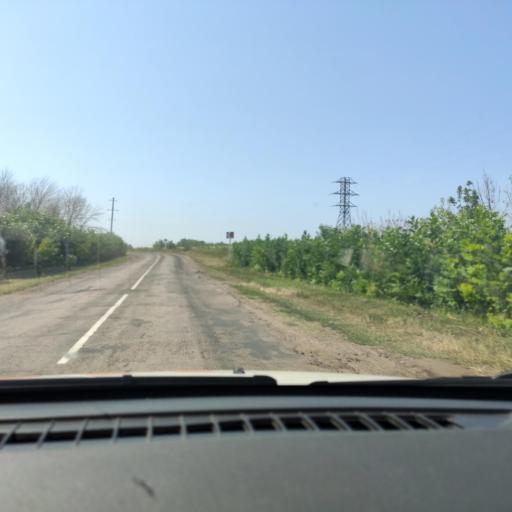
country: RU
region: Voronezj
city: Ol'khovatka
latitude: 50.5994
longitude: 39.2982
